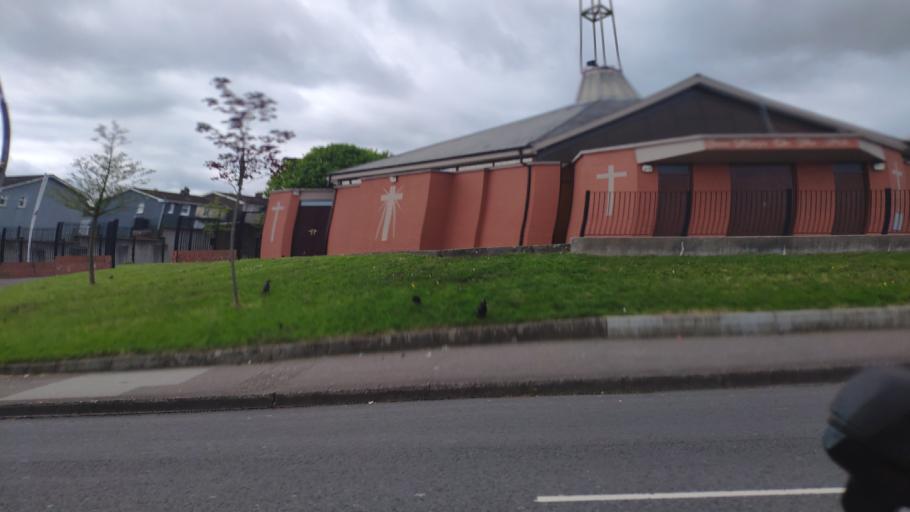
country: IE
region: Munster
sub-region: County Cork
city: Cork
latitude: 51.9039
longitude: -8.5052
